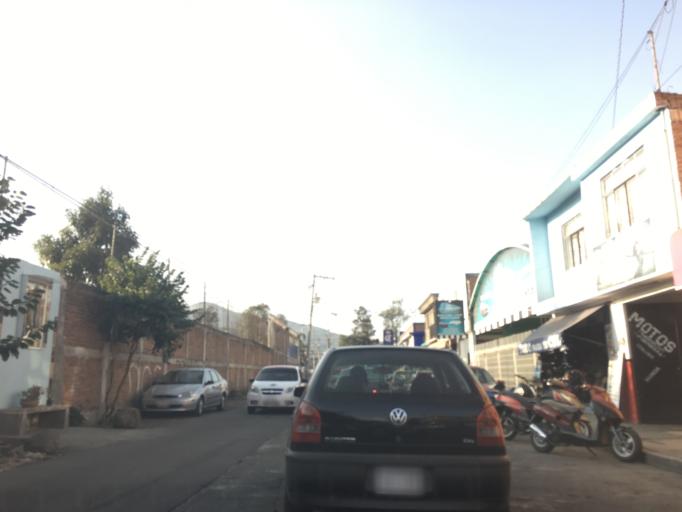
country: MX
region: Michoacan
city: Morelia
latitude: 19.7023
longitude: -101.2294
